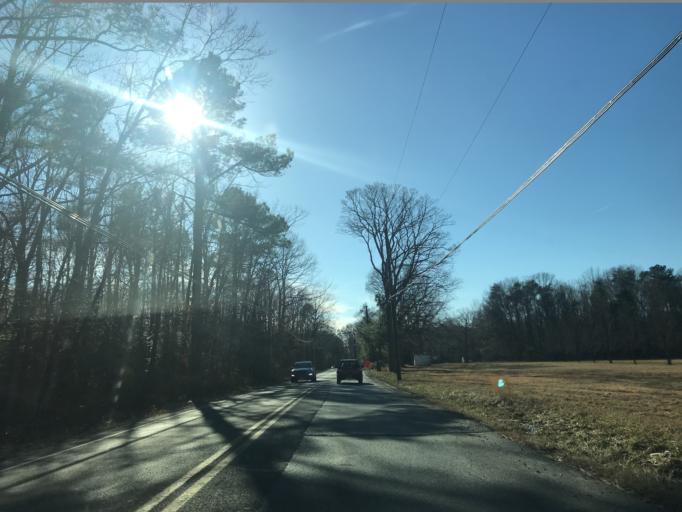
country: US
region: Maryland
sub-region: Charles County
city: Waldorf
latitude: 38.6849
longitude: -76.9240
